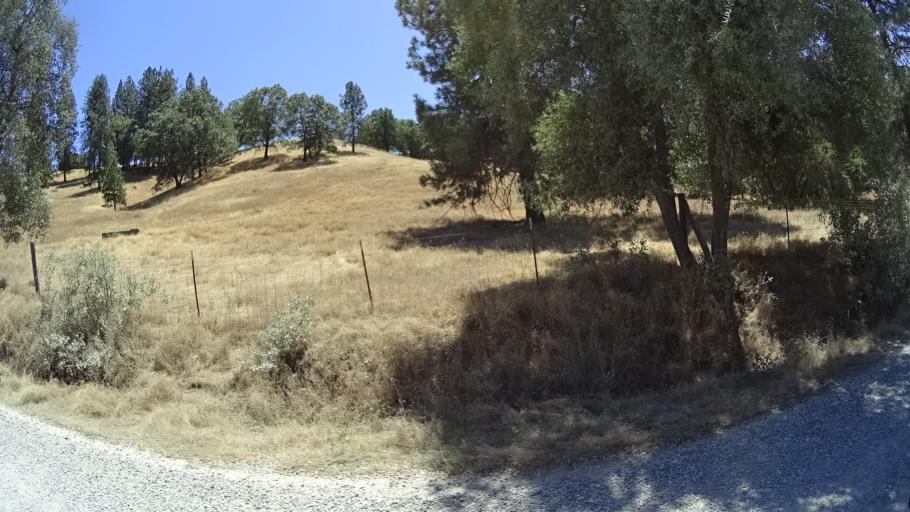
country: US
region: California
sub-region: Calaveras County
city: Murphys
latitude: 38.1094
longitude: -120.4804
